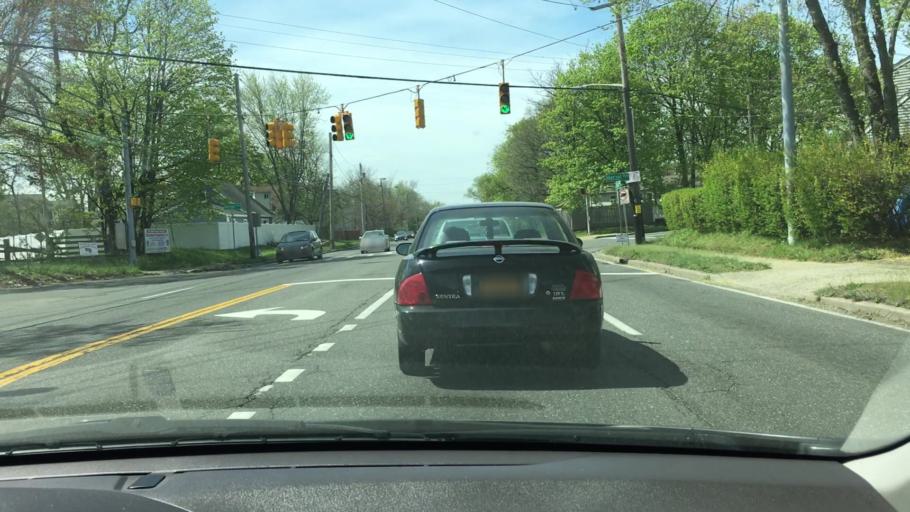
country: US
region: New York
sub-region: Suffolk County
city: North Lindenhurst
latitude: 40.7179
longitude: -73.3797
